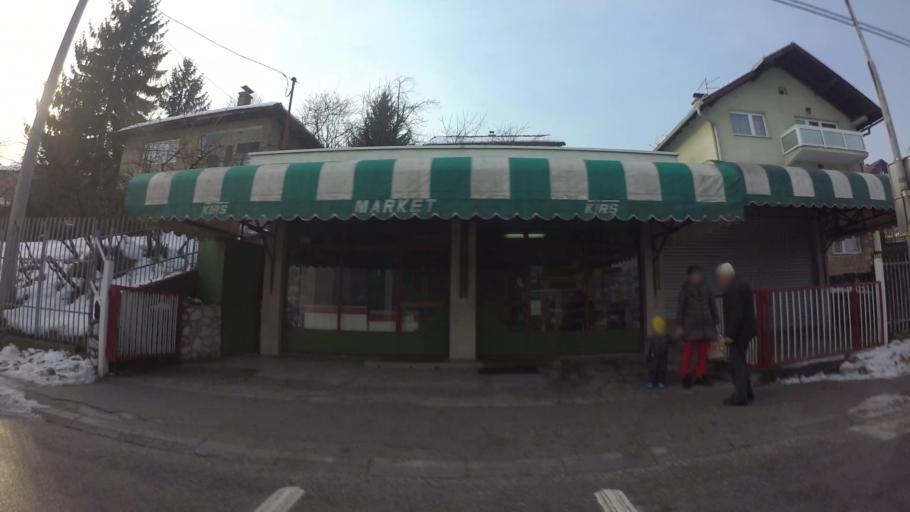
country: BA
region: Federation of Bosnia and Herzegovina
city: Kobilja Glava
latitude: 43.8714
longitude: 18.4012
